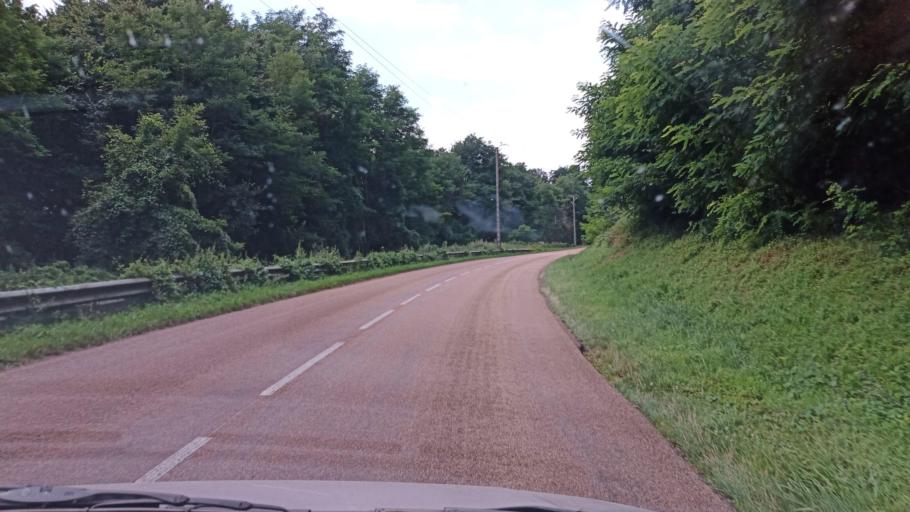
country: FR
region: Bourgogne
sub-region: Departement de l'Yonne
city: Villeneuve-sur-Yonne
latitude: 48.0633
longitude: 3.2585
